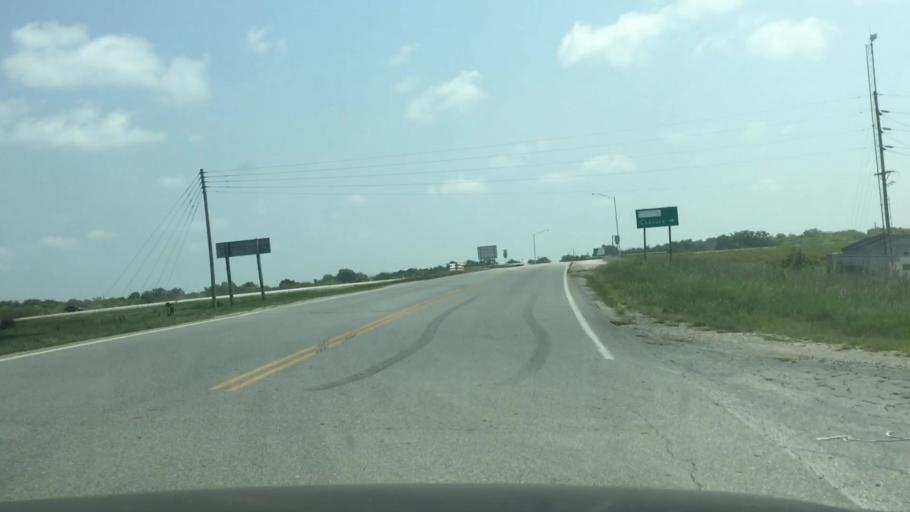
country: US
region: Kansas
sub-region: Allen County
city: Humboldt
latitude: 37.8204
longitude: -95.4126
